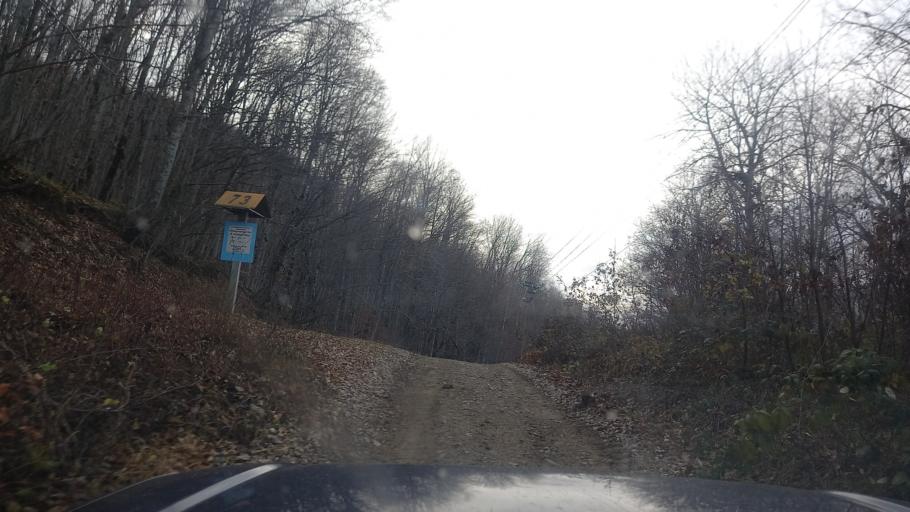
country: RU
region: Krasnodarskiy
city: Neftegorsk
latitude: 44.2178
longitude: 39.7223
